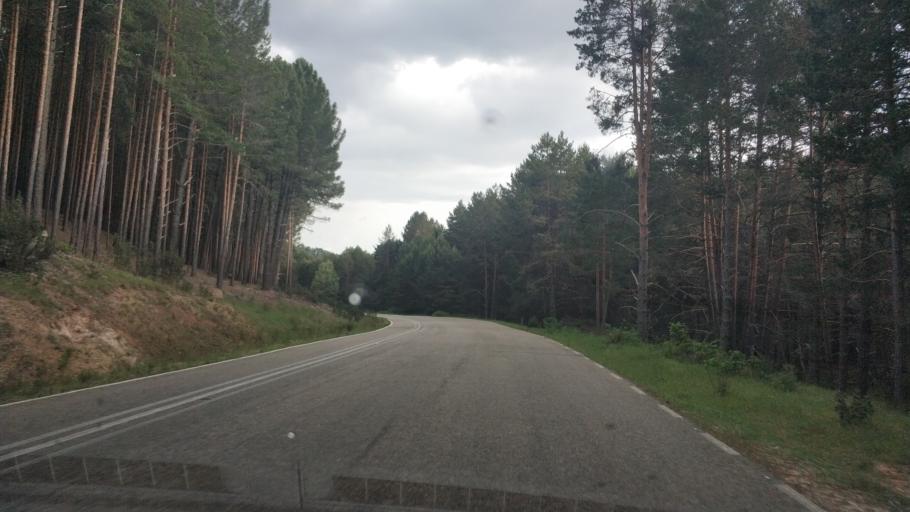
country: ES
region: Castille and Leon
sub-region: Provincia de Soria
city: San Leonardo de Yague
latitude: 41.8431
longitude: -3.0674
